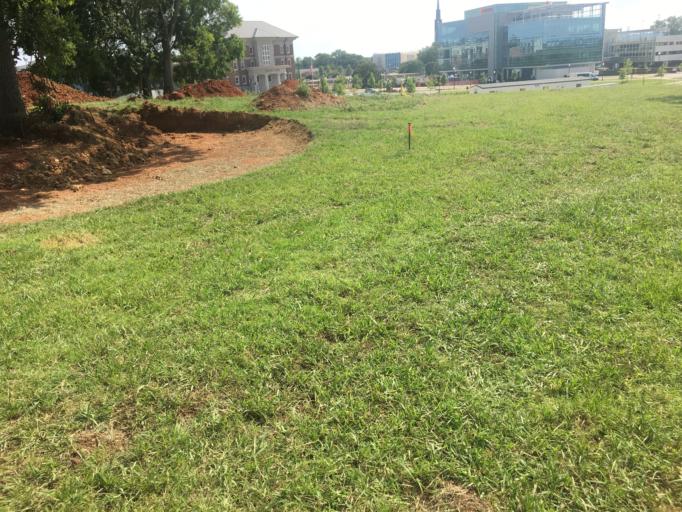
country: US
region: Alabama
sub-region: Madison County
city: Huntsville
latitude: 34.7249
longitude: -86.5842
